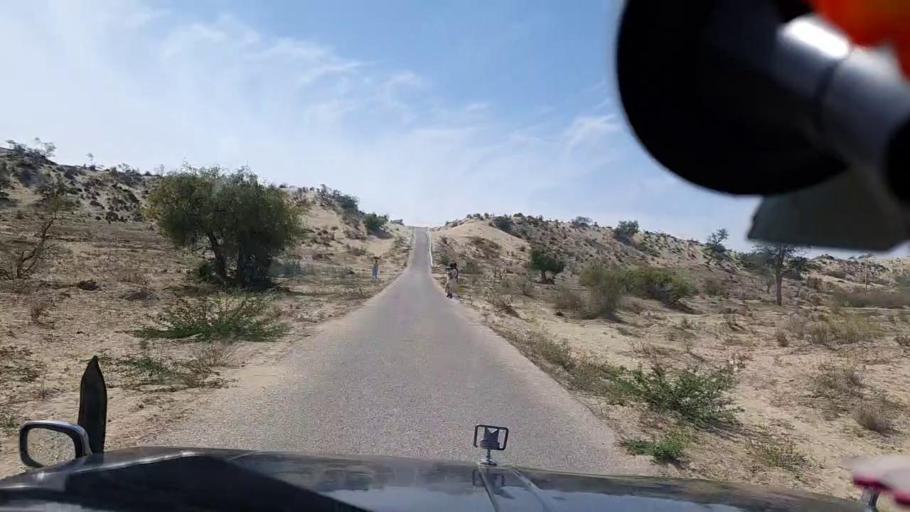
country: PK
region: Sindh
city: Diplo
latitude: 24.3963
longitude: 69.5886
